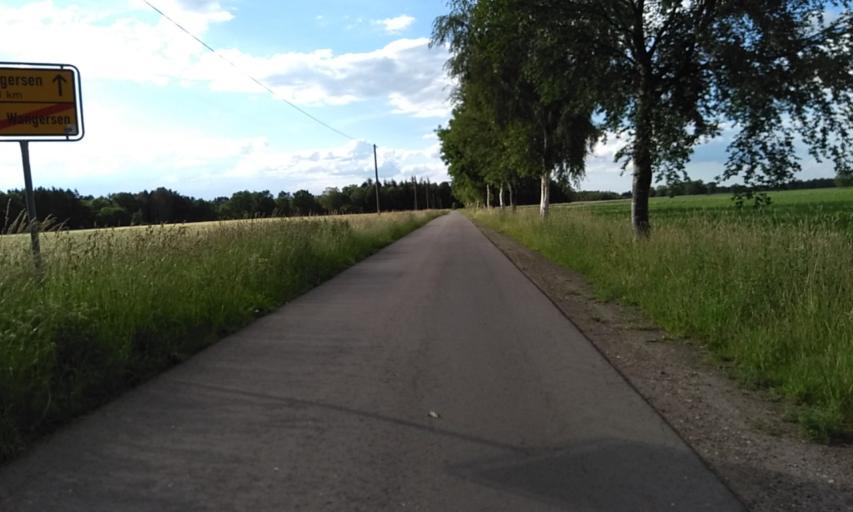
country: DE
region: Lower Saxony
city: Vierden
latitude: 53.3580
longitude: 9.4656
